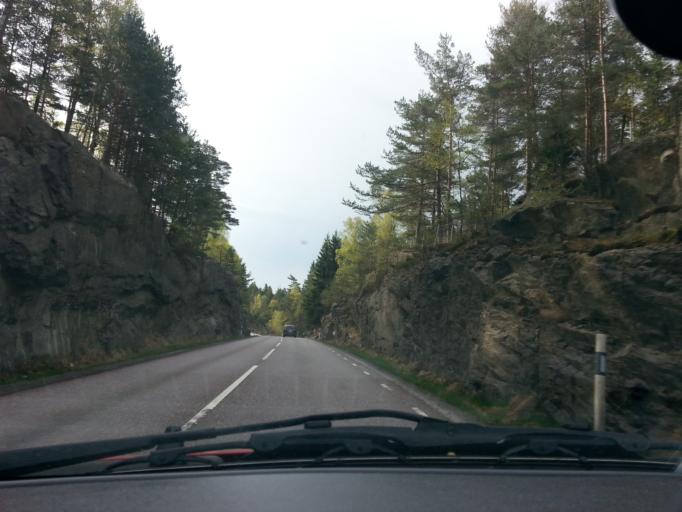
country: SE
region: Vaestra Goetaland
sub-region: Partille Kommun
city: Furulund
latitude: 57.6954
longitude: 12.1570
